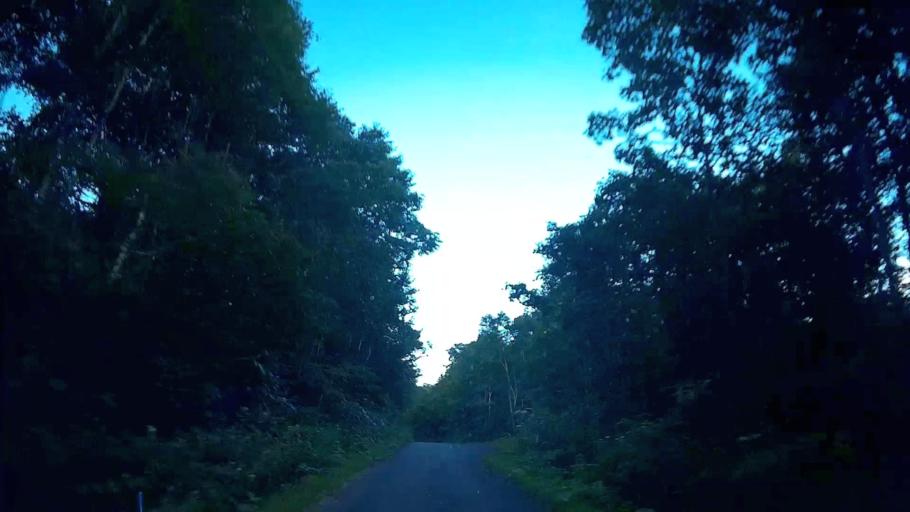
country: JP
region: Hokkaido
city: Iwanai
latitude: 42.6016
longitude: 139.9681
